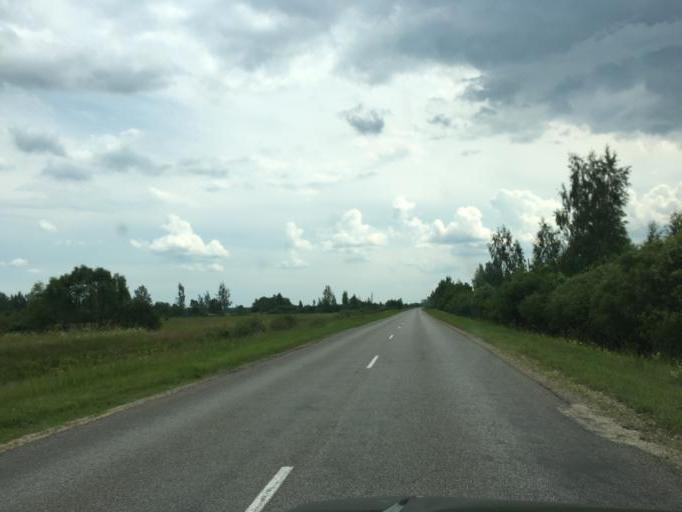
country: LV
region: Rugaju
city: Rugaji
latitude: 56.9263
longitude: 27.0693
